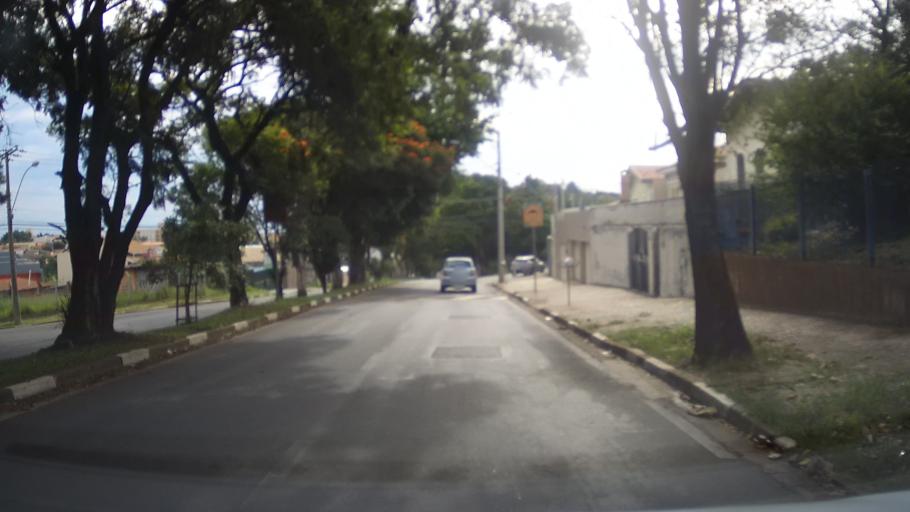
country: BR
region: Sao Paulo
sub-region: Campinas
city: Campinas
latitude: -22.8991
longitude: -47.0986
